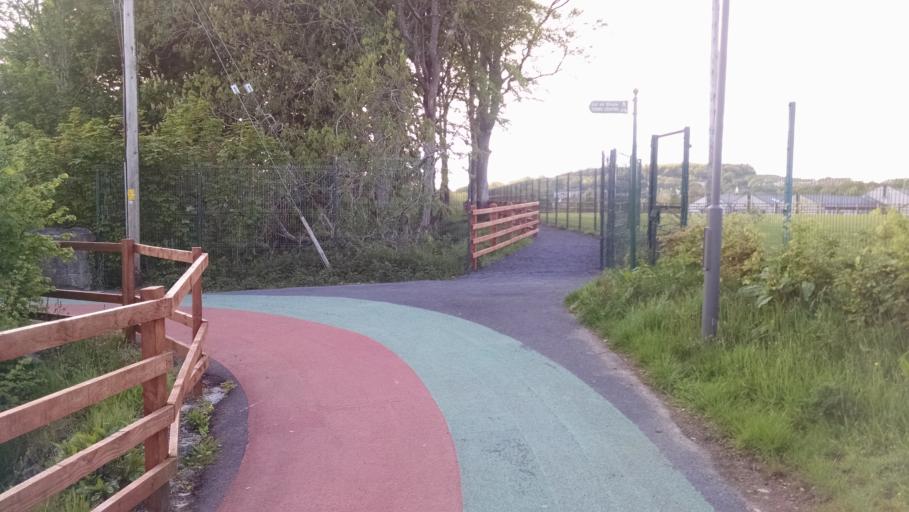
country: IE
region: Connaught
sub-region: Maigh Eo
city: Westport
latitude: 53.8000
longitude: -9.5120
